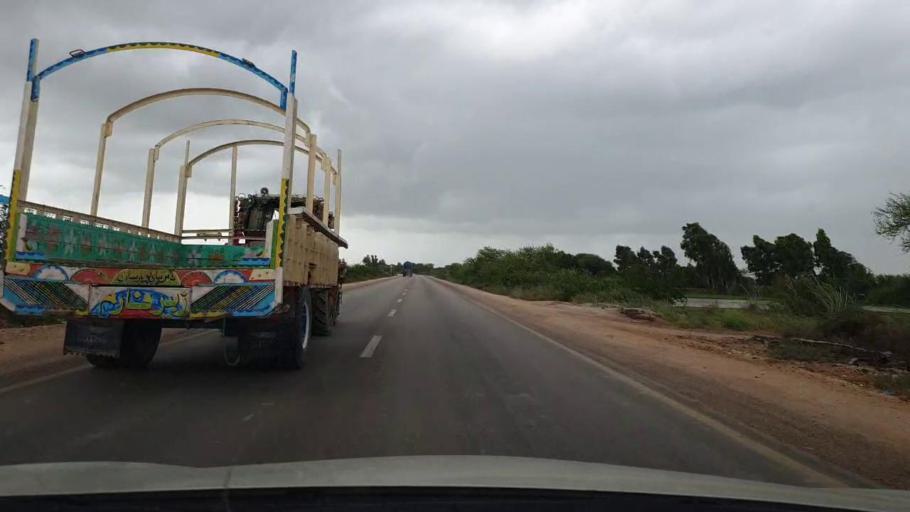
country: PK
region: Sindh
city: Kario
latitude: 24.6426
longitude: 68.4619
